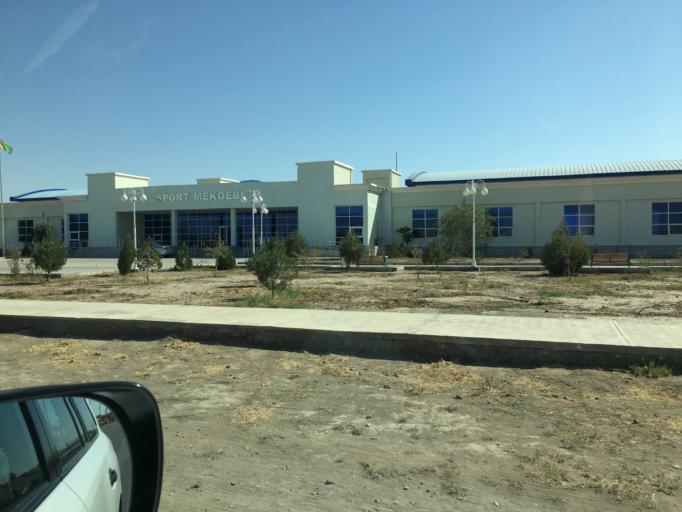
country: IR
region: Razavi Khorasan
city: Sarakhs
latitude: 36.5238
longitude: 61.2197
